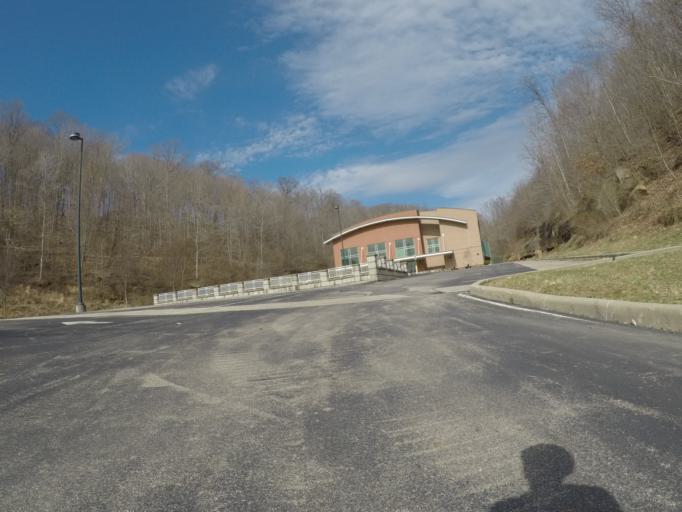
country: US
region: West Virginia
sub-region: Cabell County
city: Huntington
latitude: 38.3997
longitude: -82.4556
